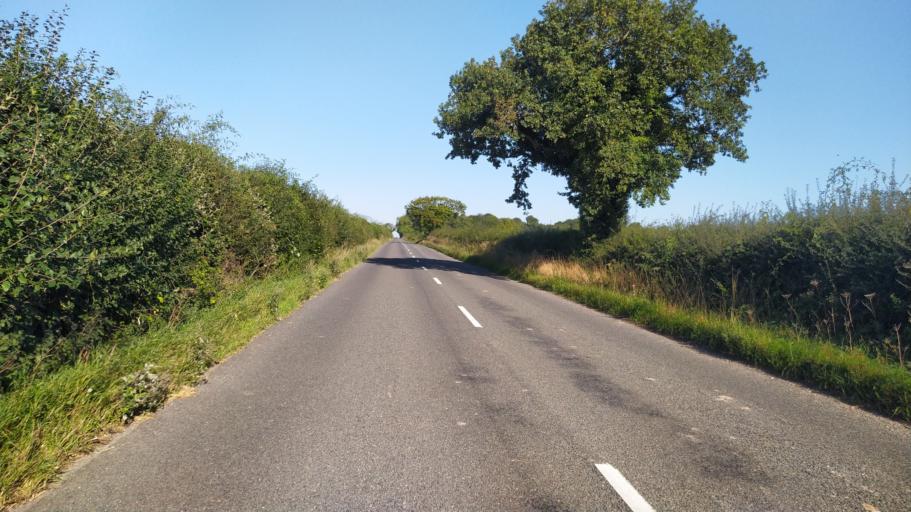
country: GB
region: England
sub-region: Hampshire
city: Abbotts Ann
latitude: 51.1546
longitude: -1.5523
